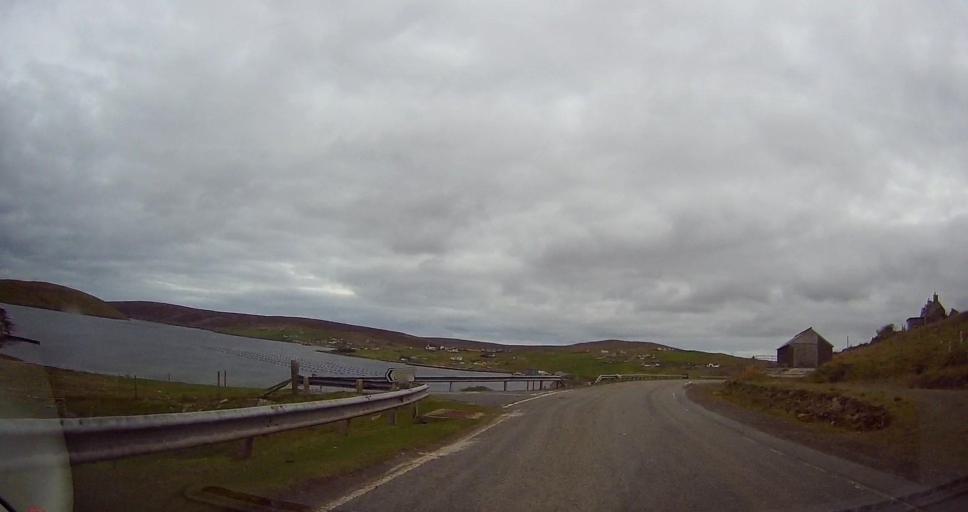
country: GB
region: Scotland
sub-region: Shetland Islands
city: Shetland
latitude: 60.6124
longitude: -1.0738
